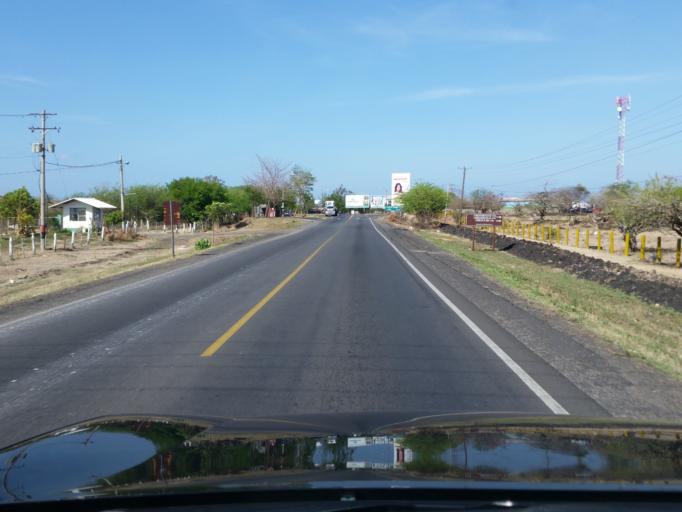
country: NI
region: Leon
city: La Paz Centro
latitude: 12.2695
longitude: -86.7346
